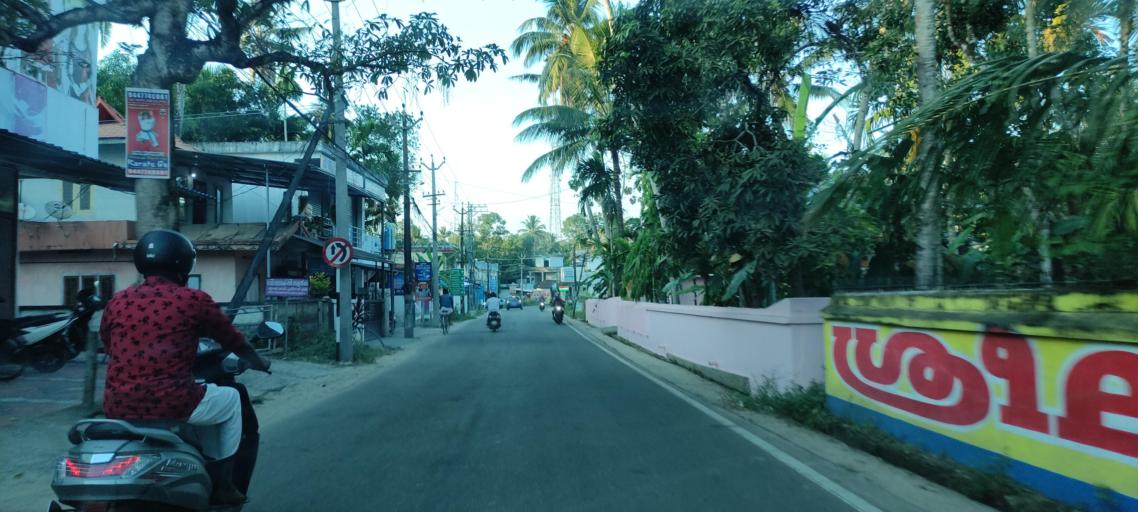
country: IN
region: Kerala
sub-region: Alappuzha
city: Kayankulam
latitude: 9.2112
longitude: 76.4615
